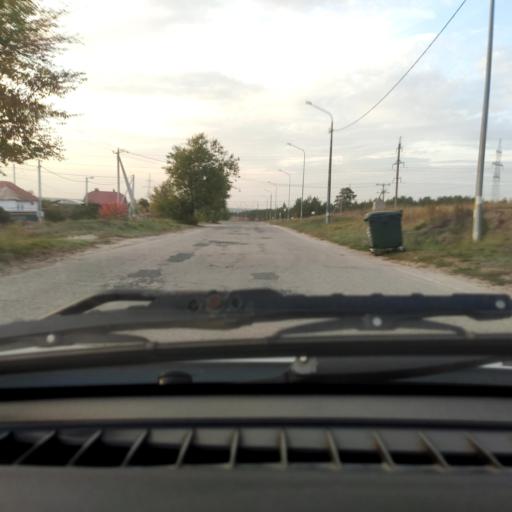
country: RU
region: Samara
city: Zhigulevsk
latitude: 53.4855
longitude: 49.5380
